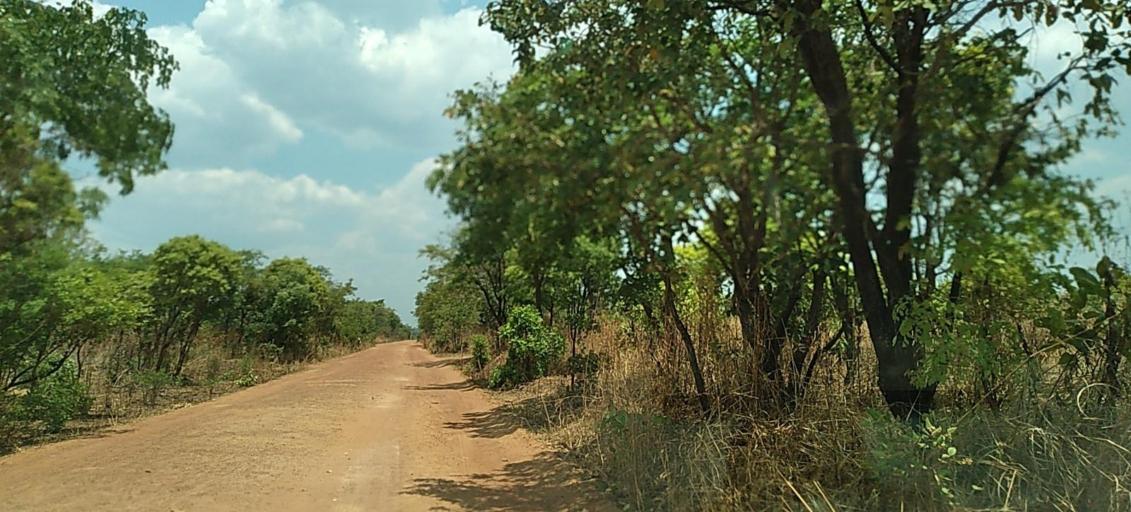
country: ZM
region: Copperbelt
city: Luanshya
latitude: -13.3828
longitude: 28.4381
